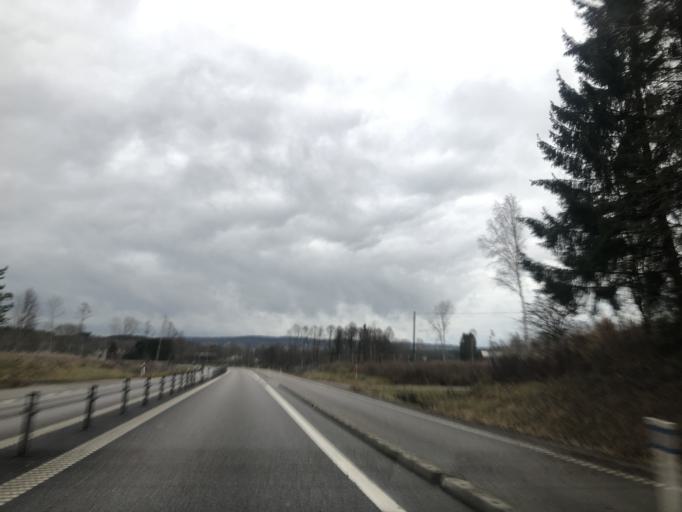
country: SE
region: Vaestra Goetaland
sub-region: Ulricehamns Kommun
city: Ulricehamn
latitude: 57.8016
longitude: 13.3580
